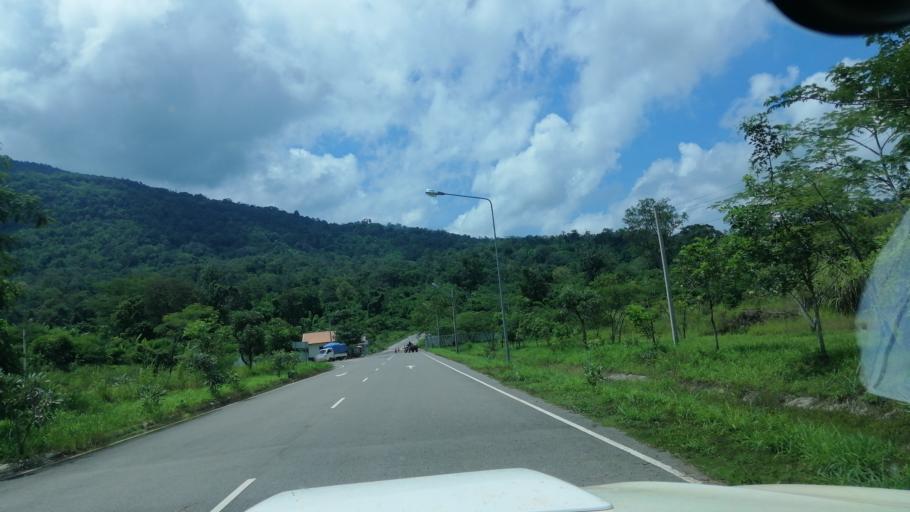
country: TH
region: Uttaradit
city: Ban Khok
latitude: 18.1087
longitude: 101.1765
